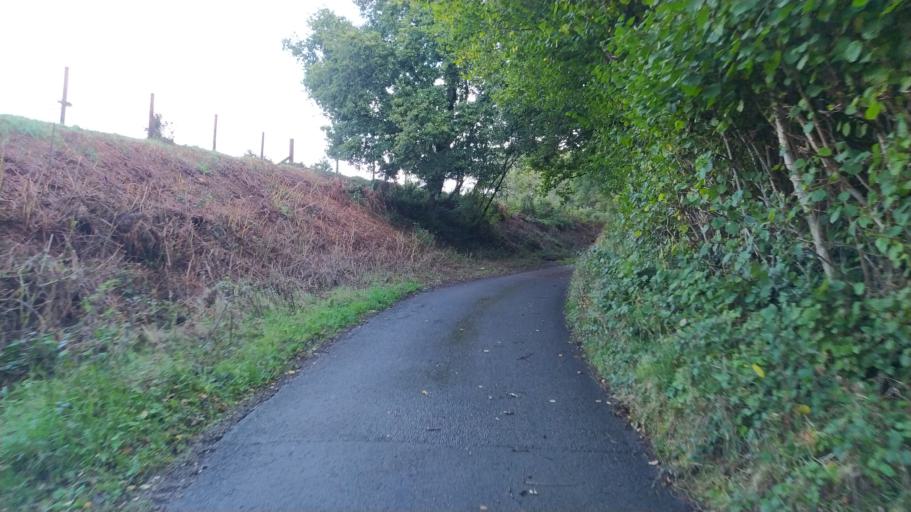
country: GB
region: England
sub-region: Dorset
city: Shaftesbury
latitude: 51.0248
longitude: -2.1355
